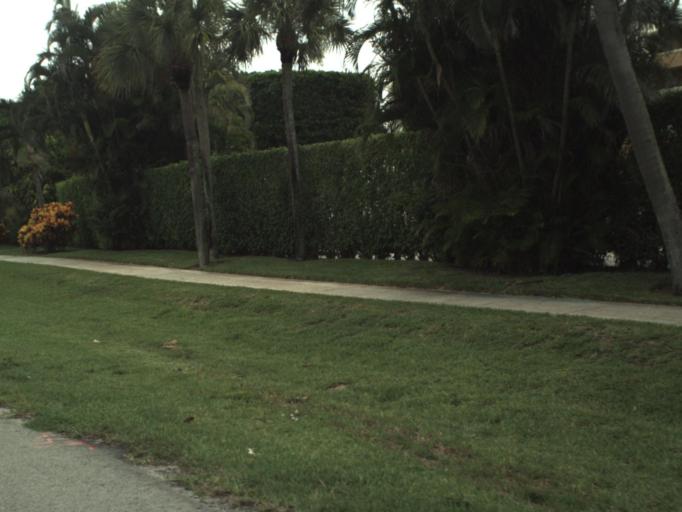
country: US
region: Florida
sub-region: Palm Beach County
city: North Palm Beach
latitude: 26.8336
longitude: -80.0599
